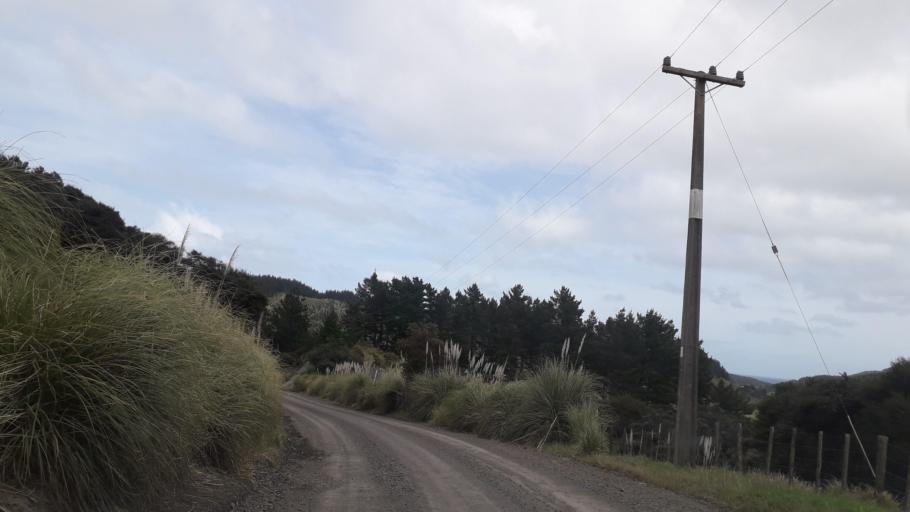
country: NZ
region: Northland
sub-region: Far North District
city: Ahipara
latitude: -35.4344
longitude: 173.3320
